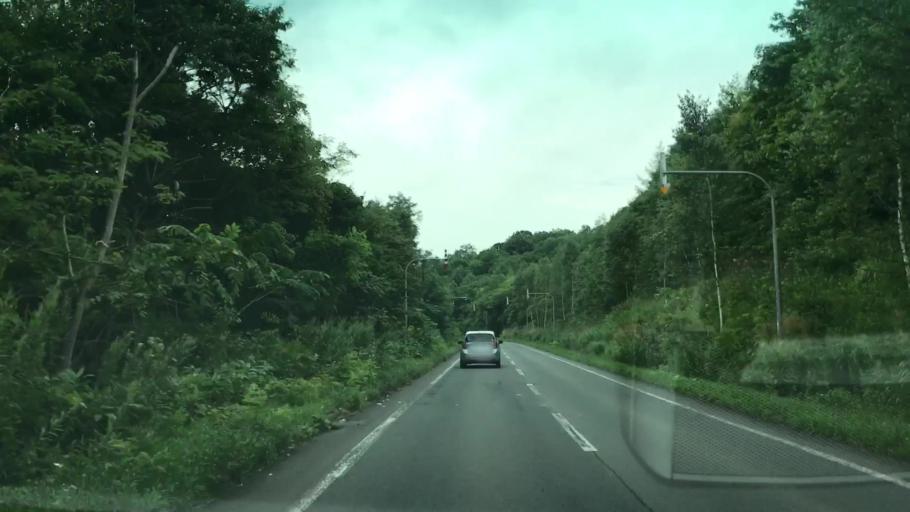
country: JP
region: Hokkaido
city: Yoichi
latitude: 43.1437
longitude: 140.8209
